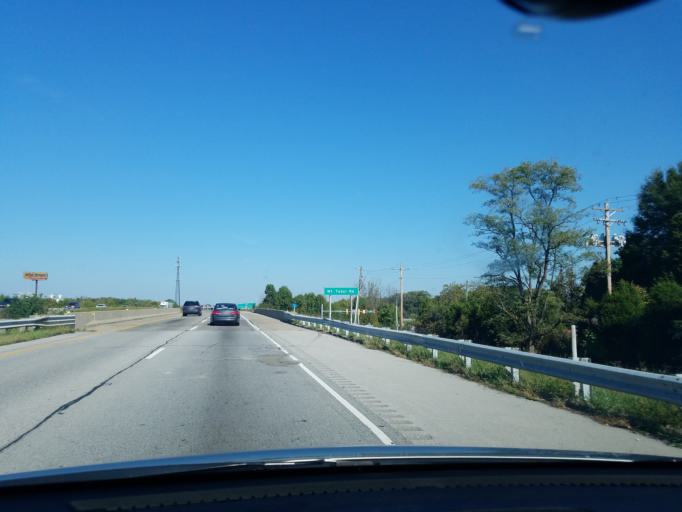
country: US
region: Indiana
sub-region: Floyd County
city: New Albany
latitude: 38.3317
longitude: -85.8258
